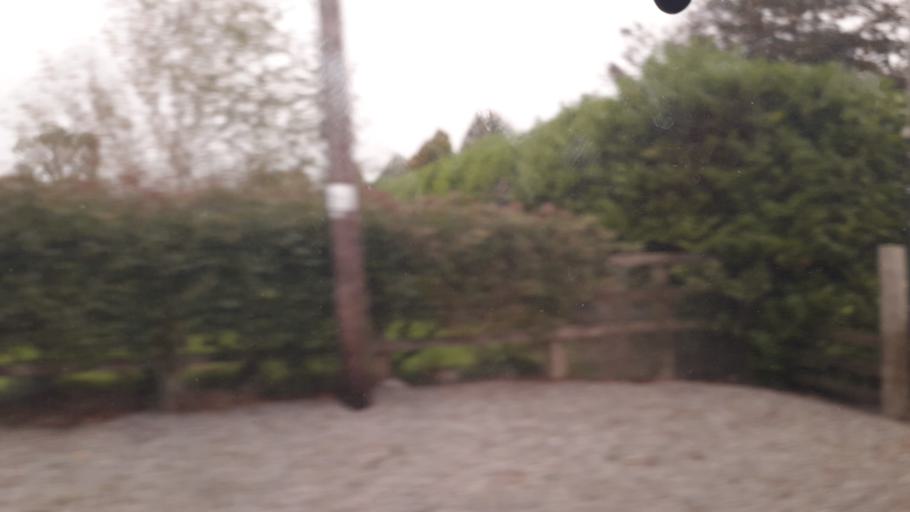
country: IE
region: Leinster
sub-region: Uibh Fhaili
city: Birr
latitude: 52.9750
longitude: -7.9710
